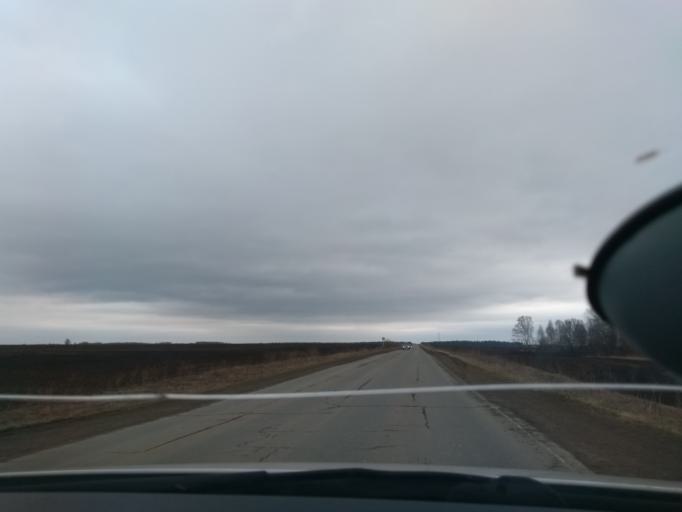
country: RU
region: Perm
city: Kungur
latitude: 57.3805
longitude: 56.8504
